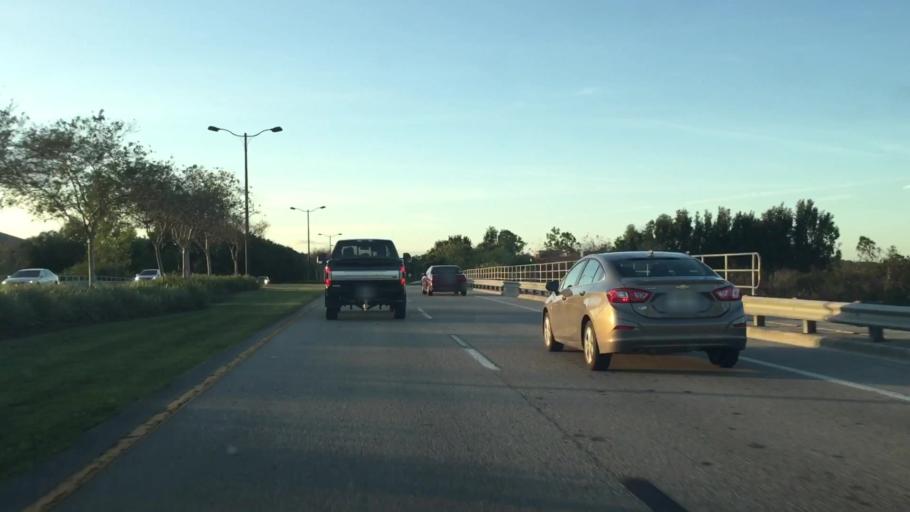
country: US
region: Florida
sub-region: Lee County
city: Three Oaks
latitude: 26.4541
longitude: -81.7754
